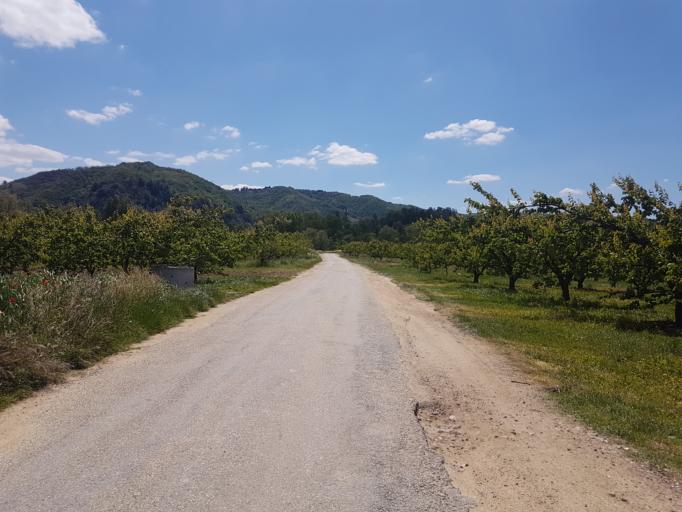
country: FR
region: Rhone-Alpes
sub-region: Departement de l'Ardeche
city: Saint-Jean-de-Muzols
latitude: 45.0805
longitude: 4.8227
